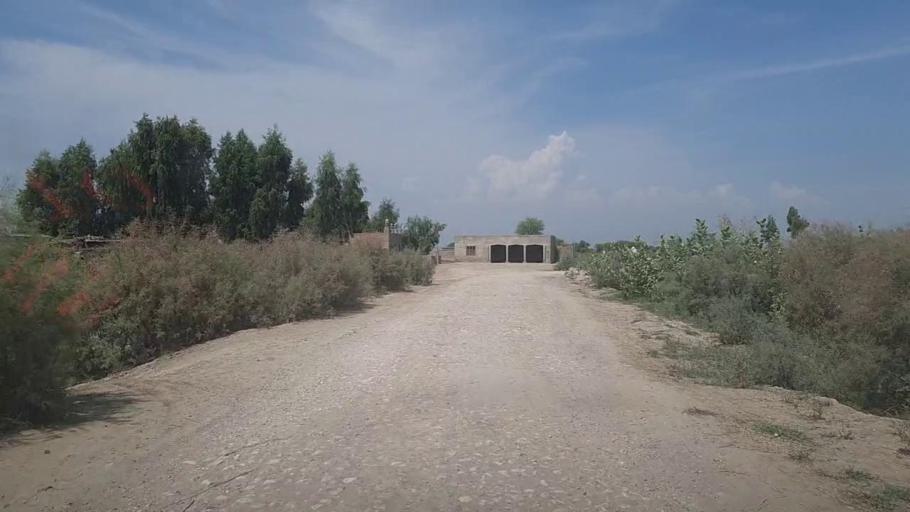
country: PK
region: Sindh
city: Kandhkot
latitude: 28.2790
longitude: 69.2345
